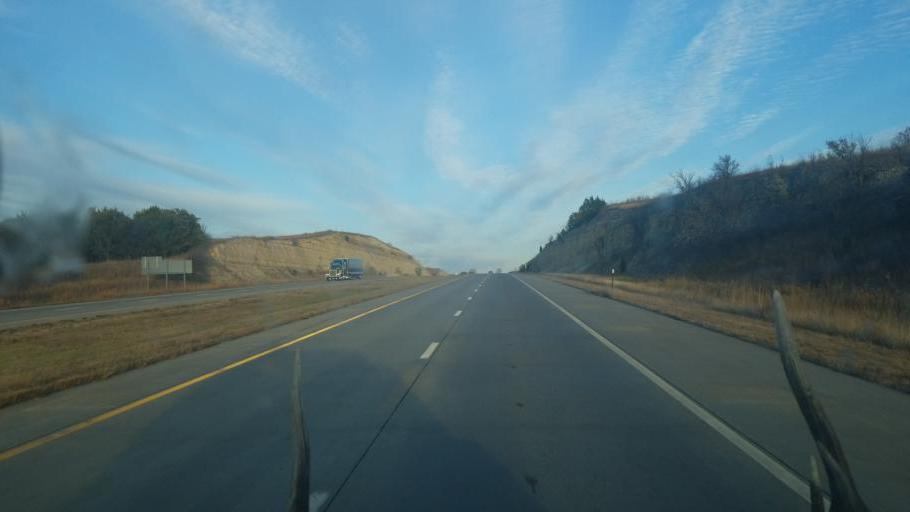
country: US
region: Kansas
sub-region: Riley County
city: Ogden
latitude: 39.0633
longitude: -96.7066
